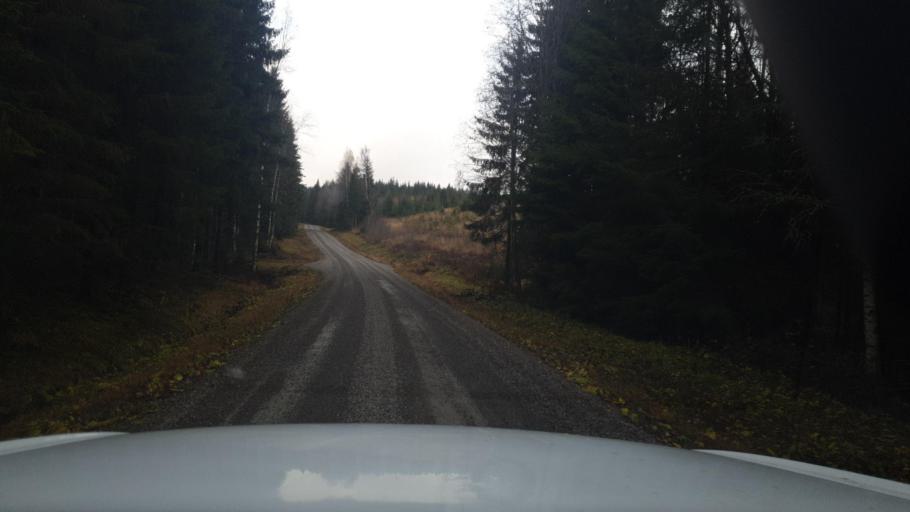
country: SE
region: Vaermland
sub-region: Eda Kommun
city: Charlottenberg
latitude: 60.0245
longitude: 12.6327
